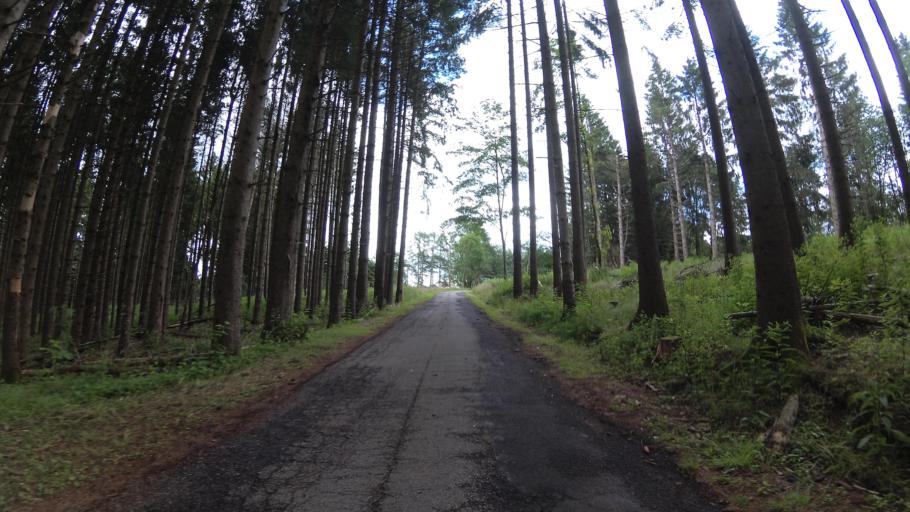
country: DE
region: Rheinland-Pfalz
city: Neuhutten
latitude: 49.5758
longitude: 7.0134
